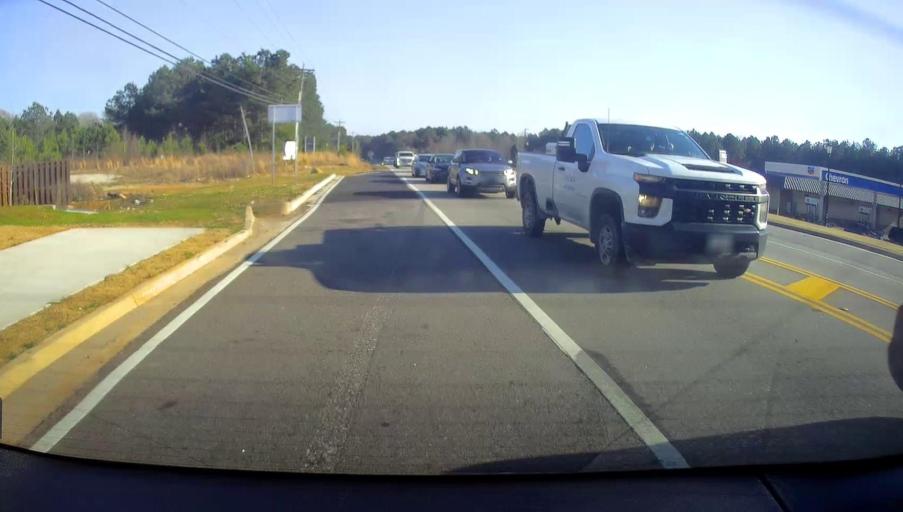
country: US
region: Georgia
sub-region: Henry County
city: Locust Grove
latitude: 33.3633
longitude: -84.1786
